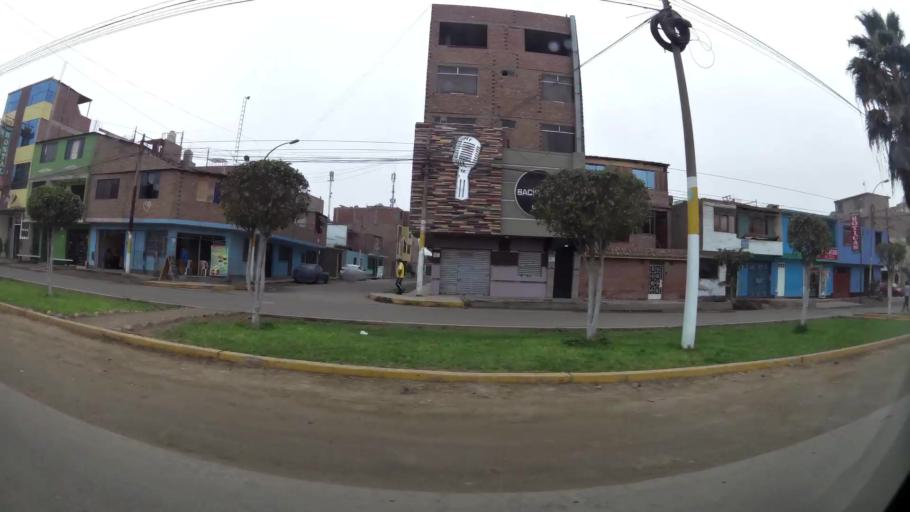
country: PE
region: Lima
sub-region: Lima
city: Carabayllo
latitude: -11.8699
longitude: -77.0726
